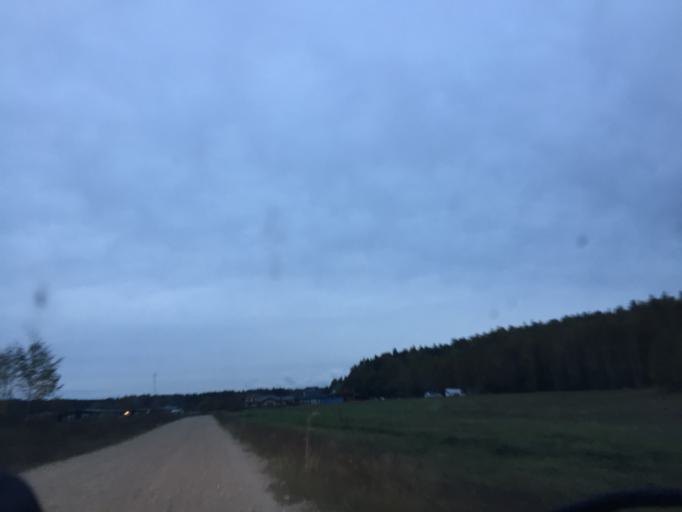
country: LV
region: Garkalne
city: Garkalne
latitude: 57.0834
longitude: 24.3801
